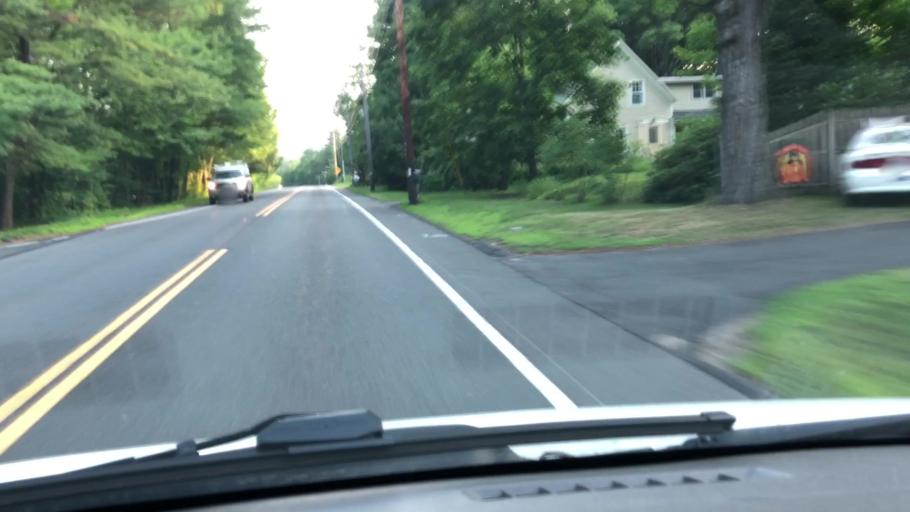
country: US
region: Massachusetts
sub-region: Hampshire County
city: Williamsburg
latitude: 42.3587
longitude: -72.6924
